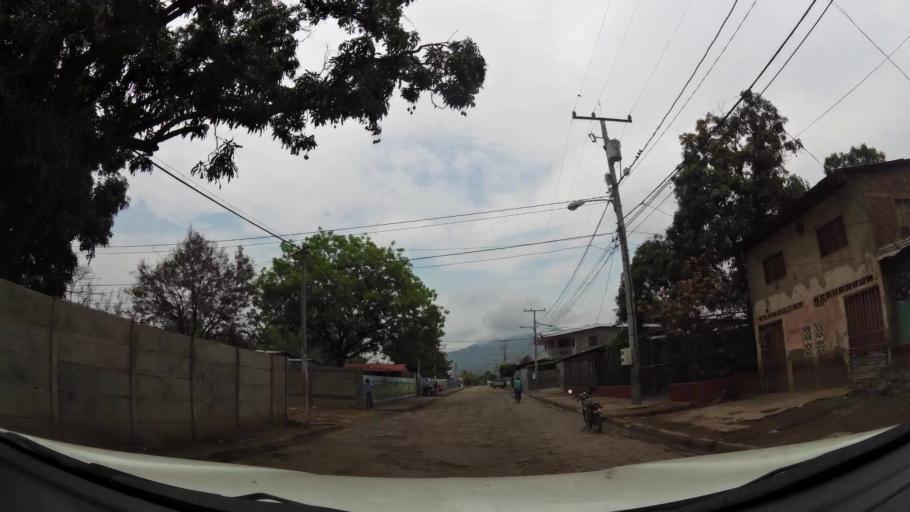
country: NI
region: Granada
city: Granada
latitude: 11.9180
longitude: -85.9551
